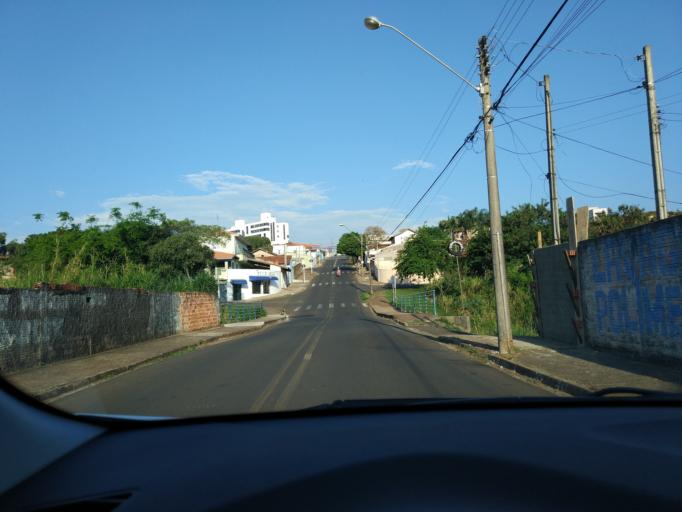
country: BR
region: Sao Paulo
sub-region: Botucatu
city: Botucatu
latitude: -22.8960
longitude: -48.4394
